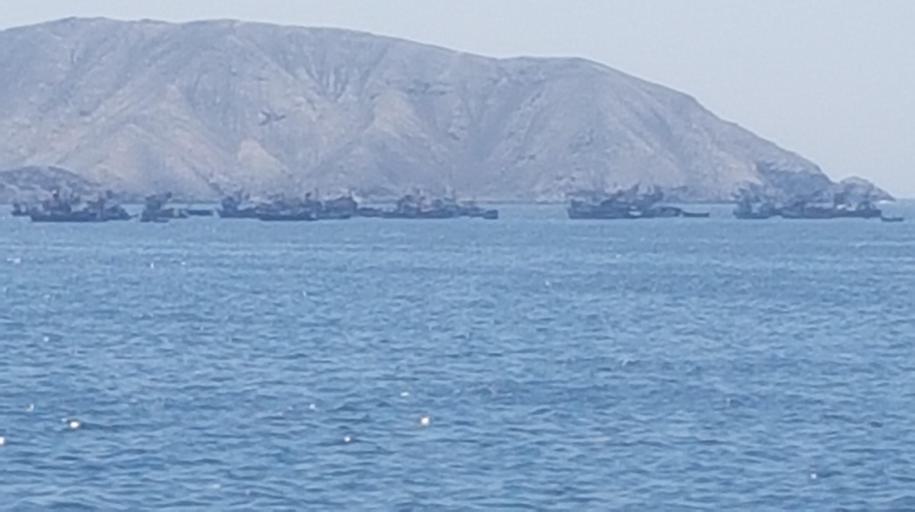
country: PE
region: Ancash
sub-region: Provincia de Santa
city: Chimbote
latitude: -9.0781
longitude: -78.5919
